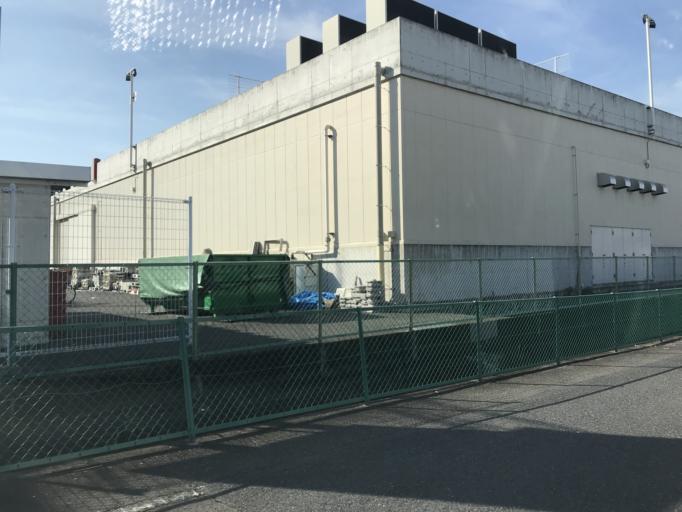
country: JP
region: Aichi
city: Iwakura
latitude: 35.2284
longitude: 136.8541
